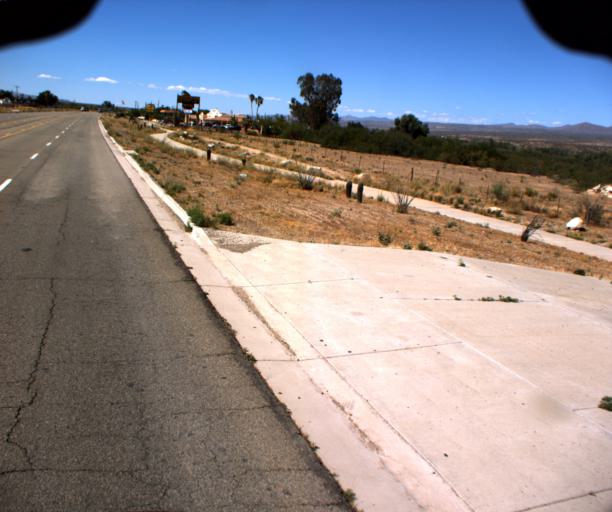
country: US
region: Arizona
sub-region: Yavapai County
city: Bagdad
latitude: 34.7018
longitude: -113.6104
